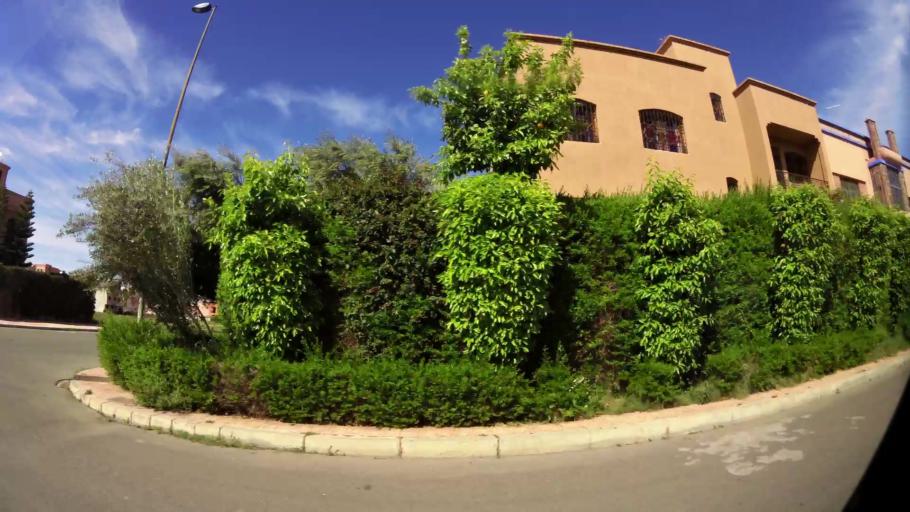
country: MA
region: Marrakech-Tensift-Al Haouz
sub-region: Marrakech
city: Marrakesh
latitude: 31.6648
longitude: -8.0294
